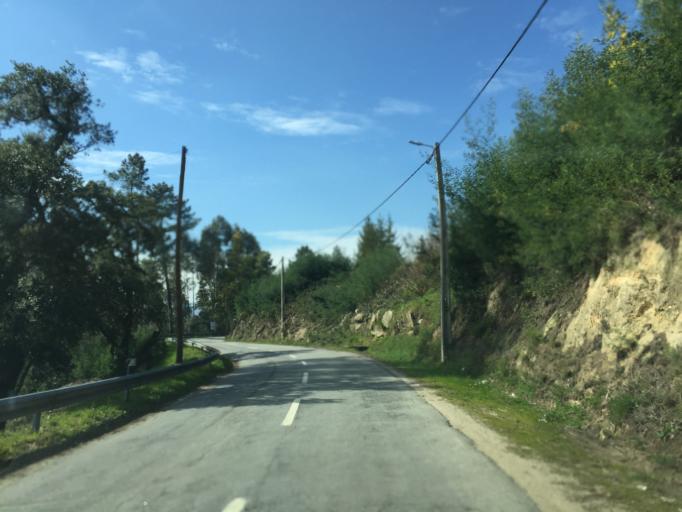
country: PT
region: Aveiro
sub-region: Castelo de Paiva
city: Castelo de Paiva
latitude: 41.0334
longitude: -8.2678
